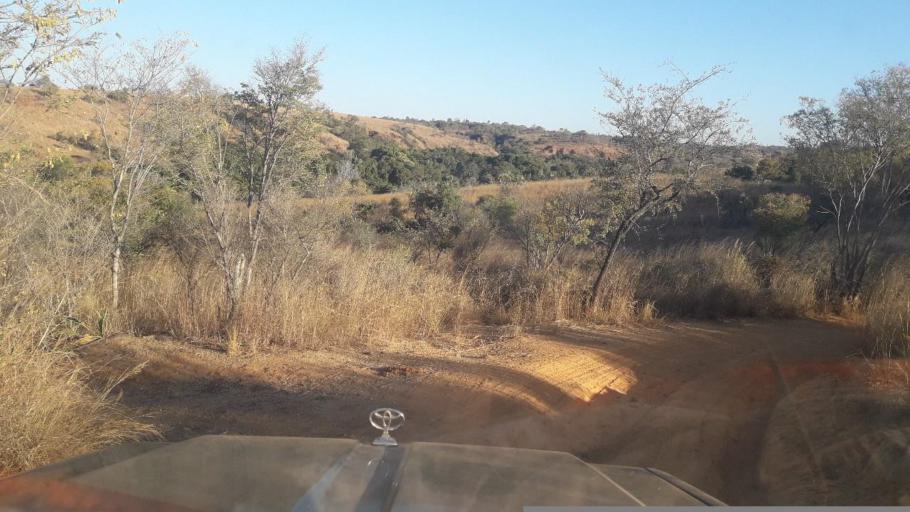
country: MG
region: Boeny
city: Sitampiky
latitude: -16.4968
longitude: 45.6079
